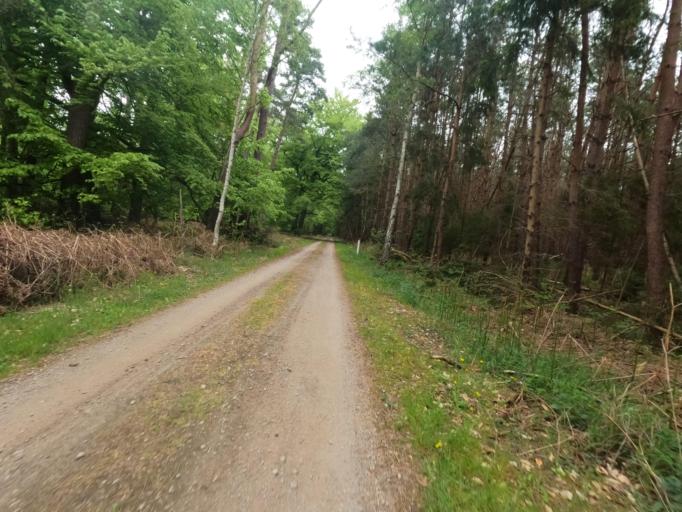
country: DE
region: Mecklenburg-Vorpommern
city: Born
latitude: 54.4112
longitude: 12.4955
